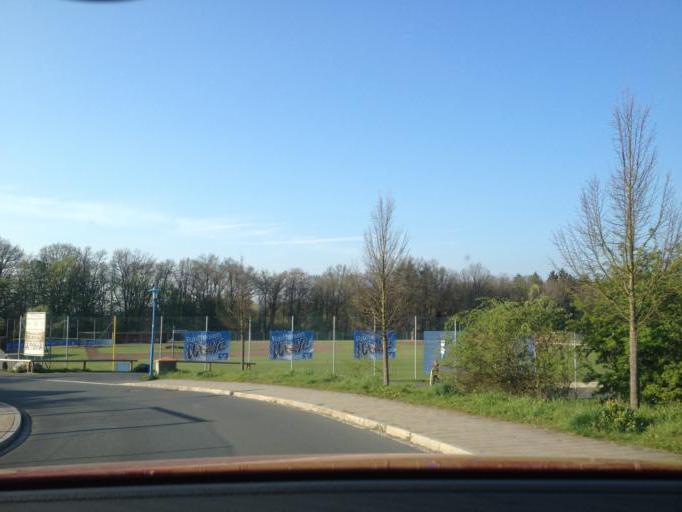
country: DE
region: Bavaria
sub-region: Regierungsbezirk Mittelfranken
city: Lauf an der Pegnitz
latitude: 49.5201
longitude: 11.2639
